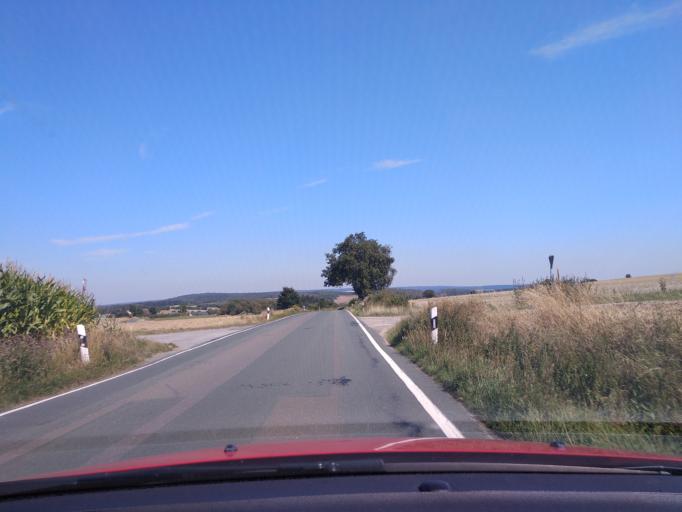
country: DE
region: North Rhine-Westphalia
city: Beverungen
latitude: 51.6759
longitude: 9.3051
